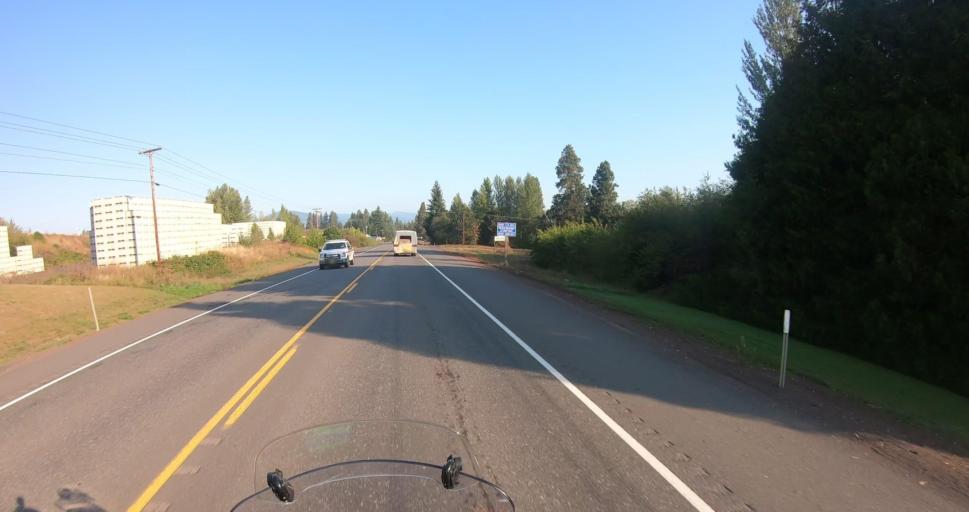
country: US
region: Oregon
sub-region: Hood River County
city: Odell
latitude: 45.6361
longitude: -121.5131
